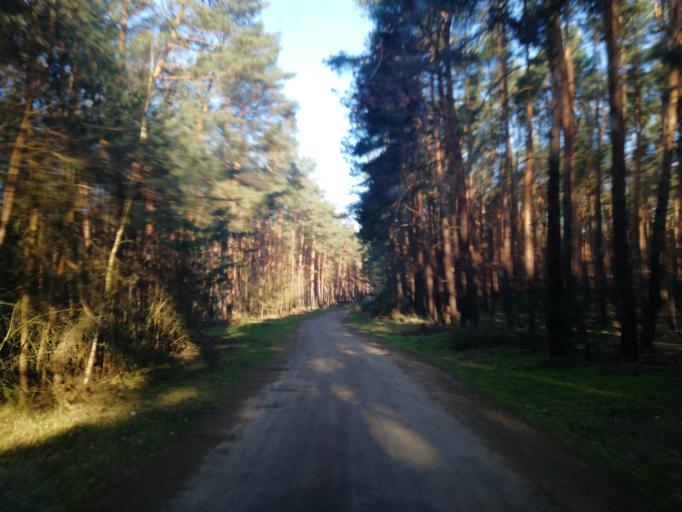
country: DE
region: Brandenburg
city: Drahnsdorf
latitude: 51.9415
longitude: 13.5767
